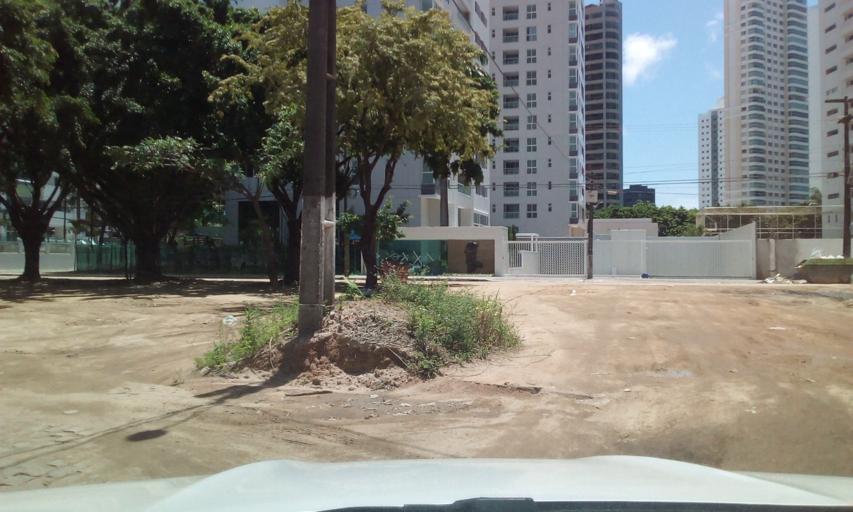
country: BR
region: Paraiba
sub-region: Joao Pessoa
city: Joao Pessoa
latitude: -7.1328
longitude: -34.8287
